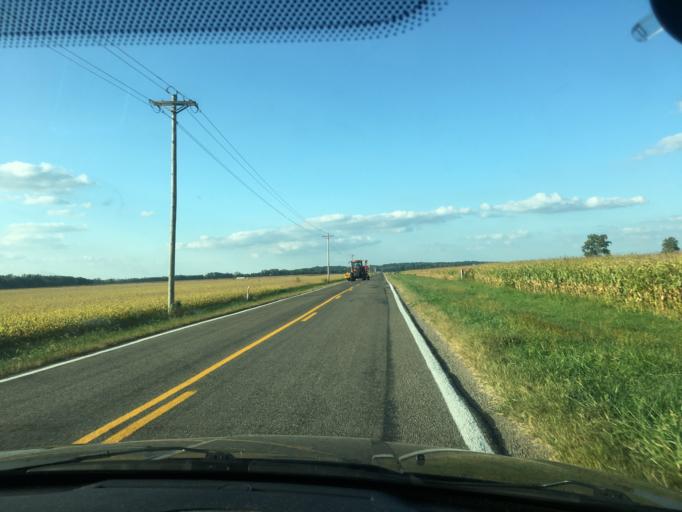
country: US
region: Ohio
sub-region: Logan County
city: West Liberty
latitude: 40.1942
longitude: -83.7810
